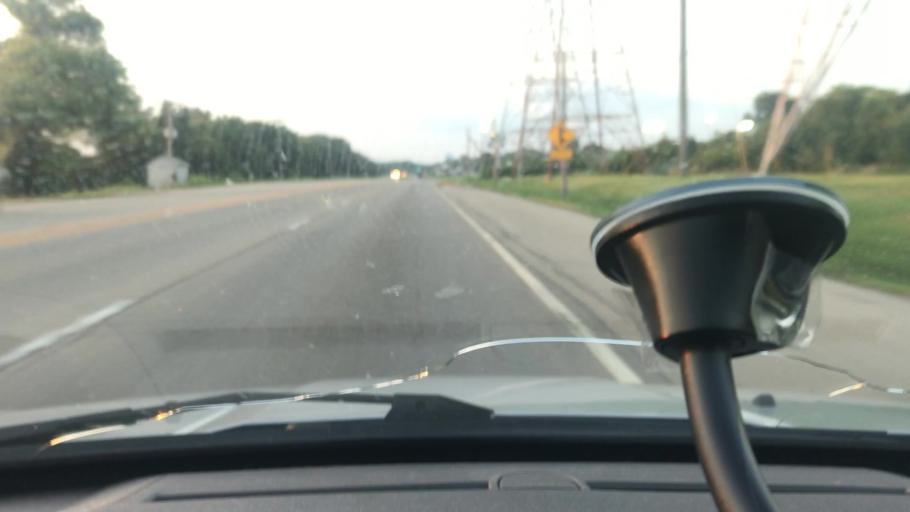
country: US
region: Illinois
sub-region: Tazewell County
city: North Pekin
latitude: 40.5952
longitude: -89.6403
